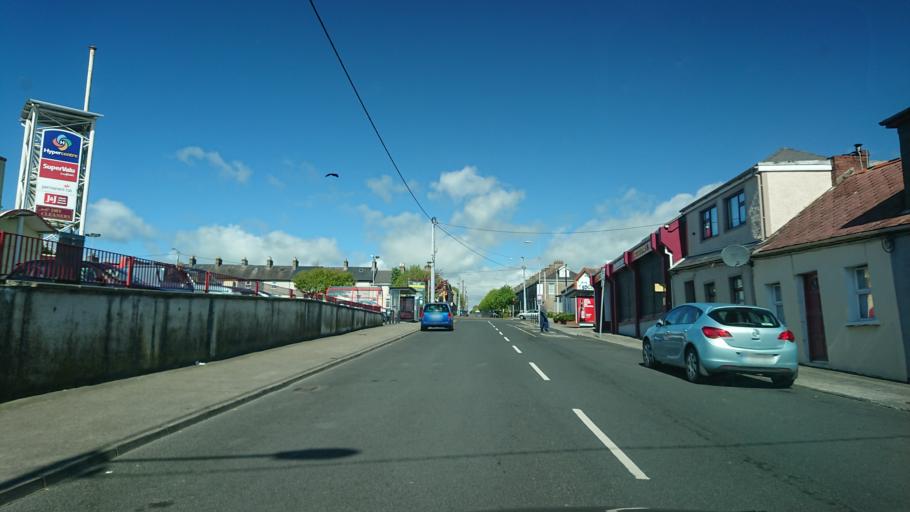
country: IE
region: Munster
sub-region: Waterford
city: Waterford
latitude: 52.2611
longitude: -7.1212
